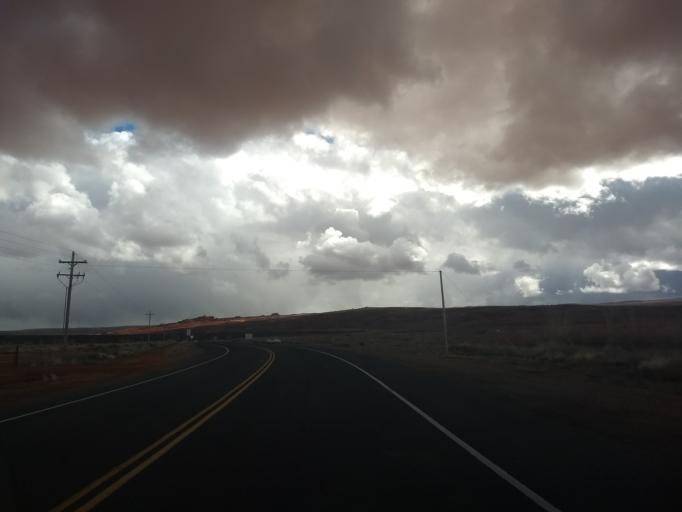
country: US
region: Utah
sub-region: Washington County
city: Washington
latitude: 37.1213
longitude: -113.3927
